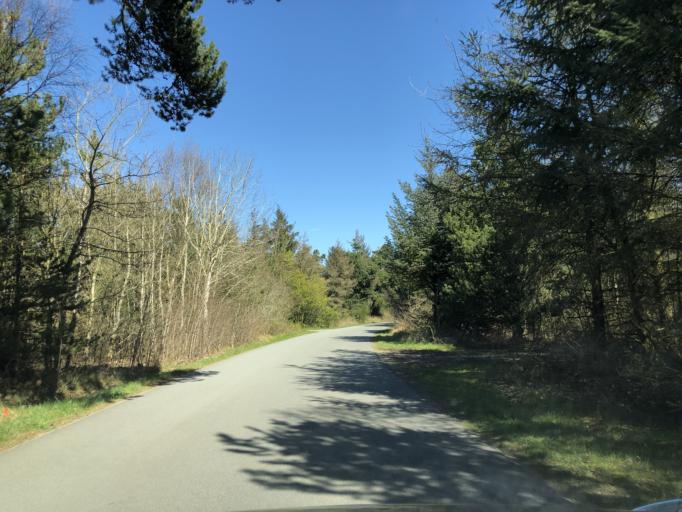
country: DK
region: Central Jutland
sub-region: Holstebro Kommune
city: Ulfborg
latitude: 56.3133
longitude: 8.1924
